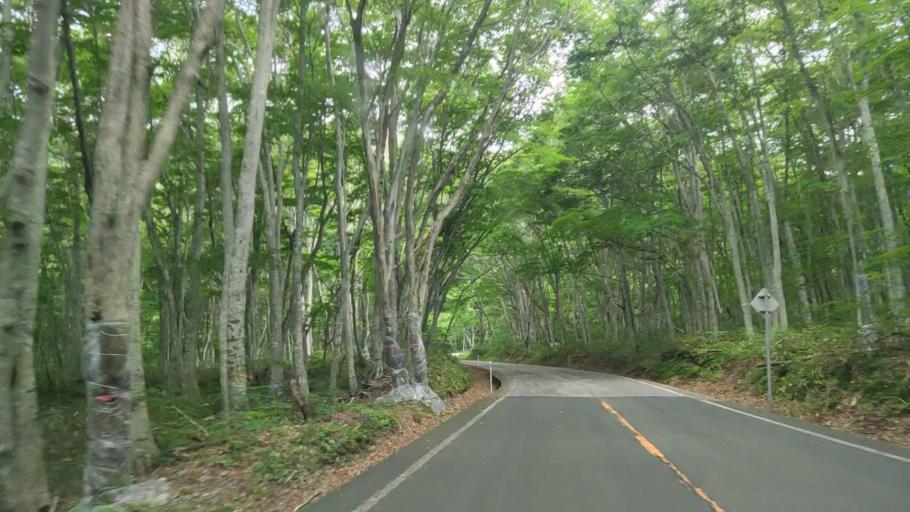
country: JP
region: Tottori
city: Yonago
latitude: 35.3465
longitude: 133.5546
